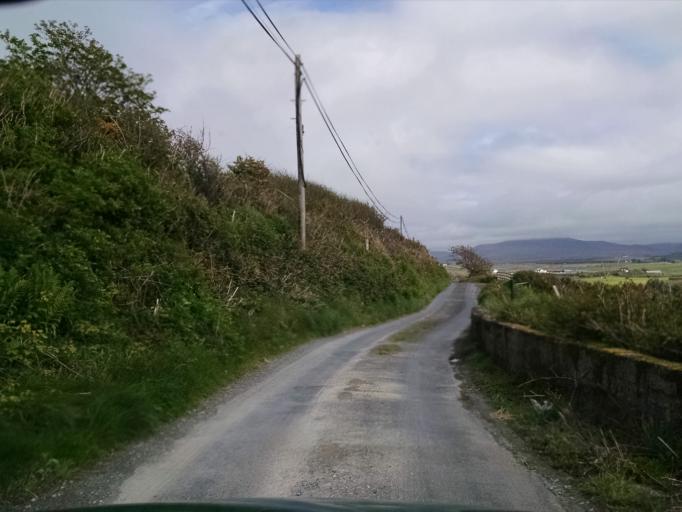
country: IE
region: Connaught
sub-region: County Galway
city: Clifden
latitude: 53.7611
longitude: -9.8516
